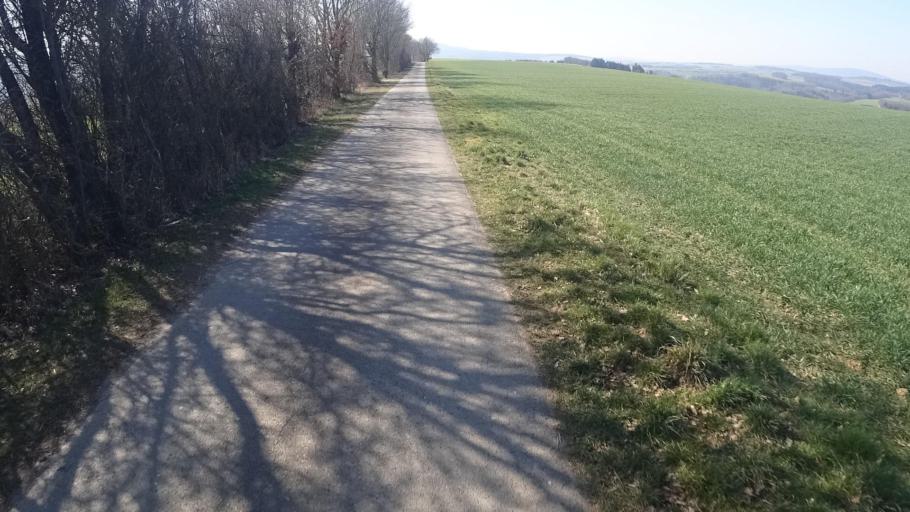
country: DE
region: Rheinland-Pfalz
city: Mengerschied
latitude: 49.9142
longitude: 7.4950
